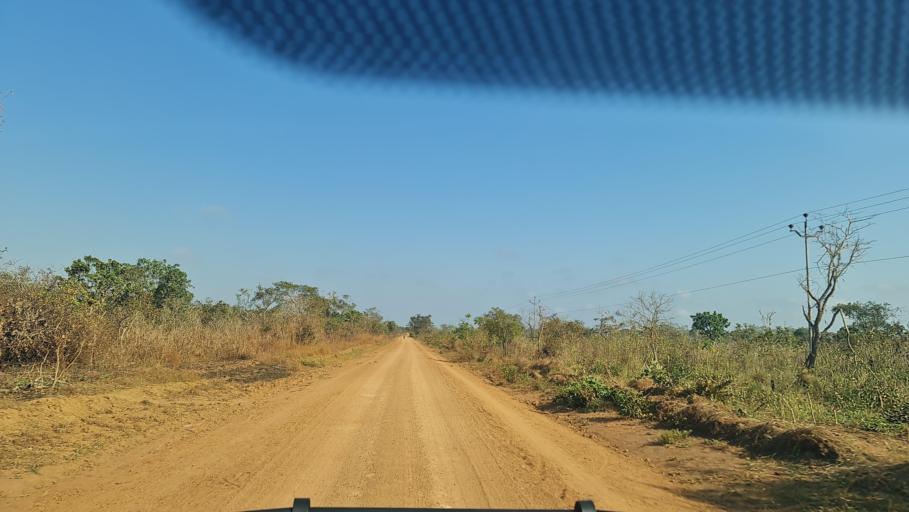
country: MZ
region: Nampula
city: Ilha de Mocambique
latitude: -15.3310
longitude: 40.1671
